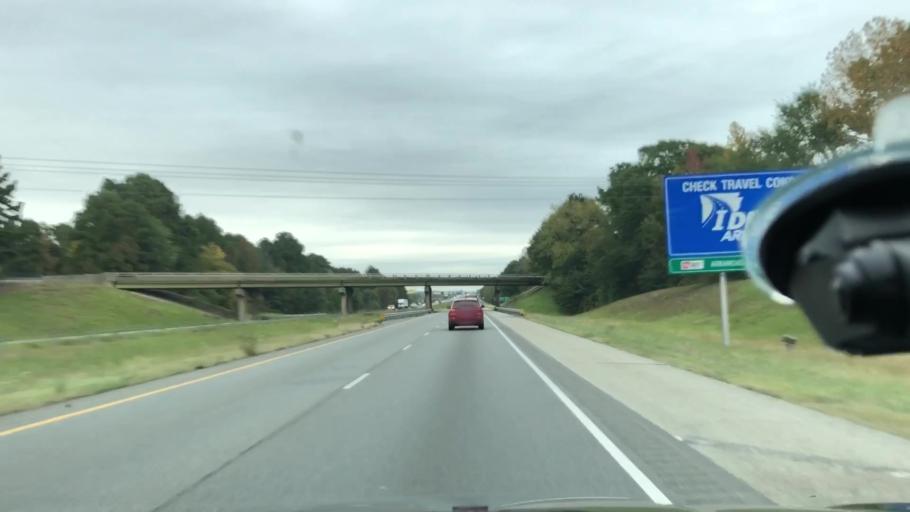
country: US
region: Arkansas
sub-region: Miller County
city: Texarkana
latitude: 33.4871
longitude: -93.9740
